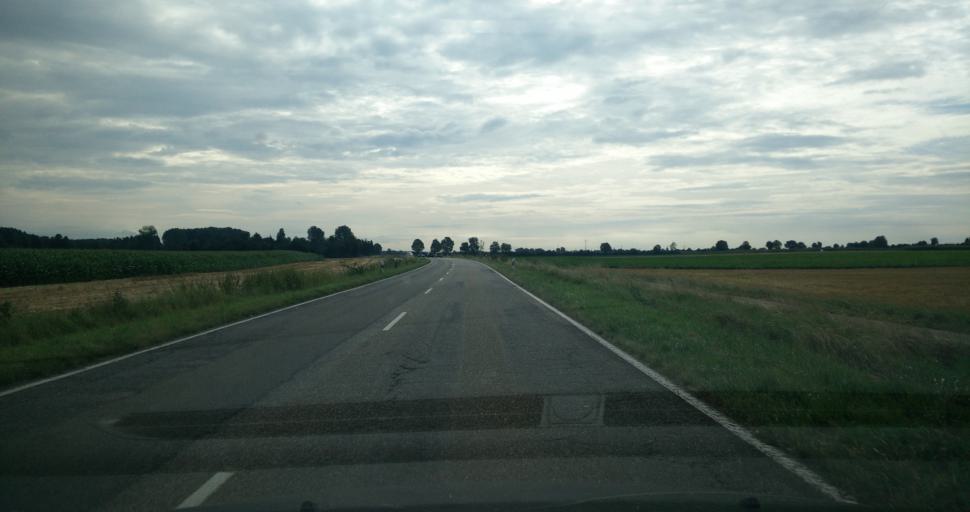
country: DE
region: Rheinland-Pfalz
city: Minfeld
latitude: 49.0925
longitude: 8.1479
